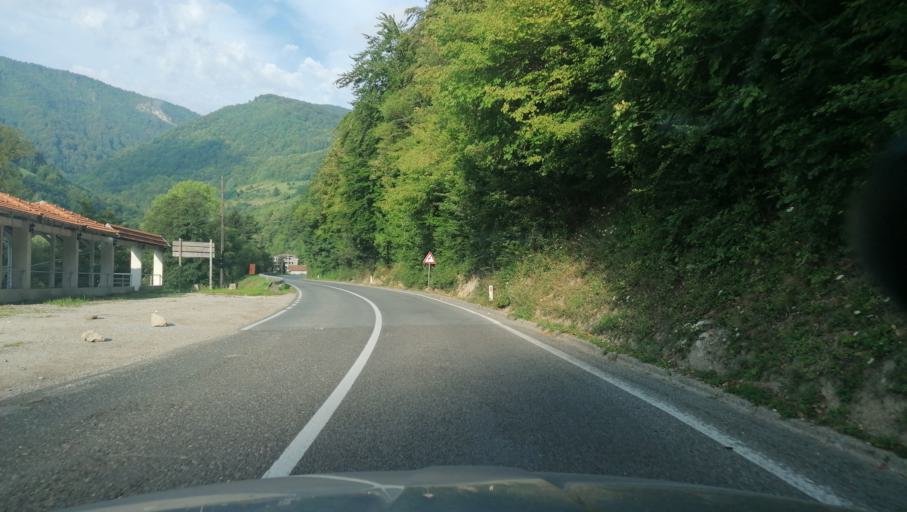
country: BA
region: Federation of Bosnia and Herzegovina
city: Jajce
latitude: 44.2331
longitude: 17.3119
